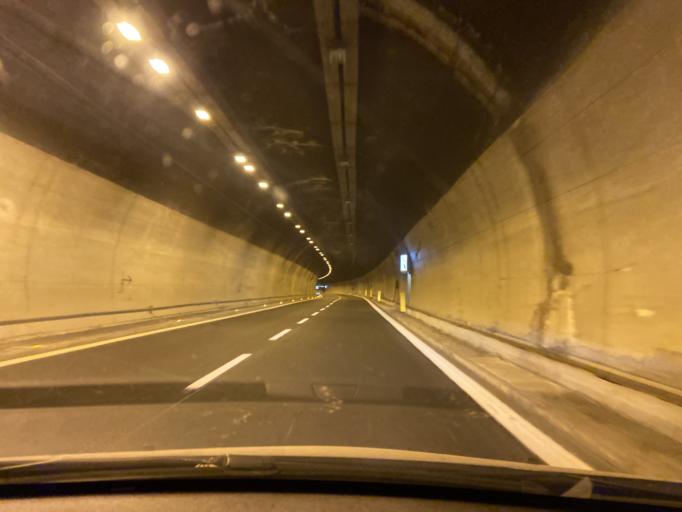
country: IT
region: Piedmont
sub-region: Provincia di Torino
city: Salbertrand
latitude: 45.0873
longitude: 6.9054
